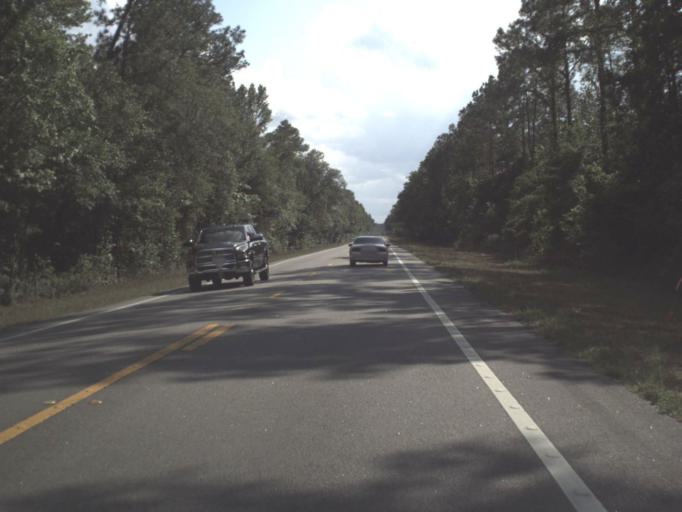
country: US
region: Florida
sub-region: Hernando County
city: Ridge Manor
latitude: 28.5288
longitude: -82.0934
